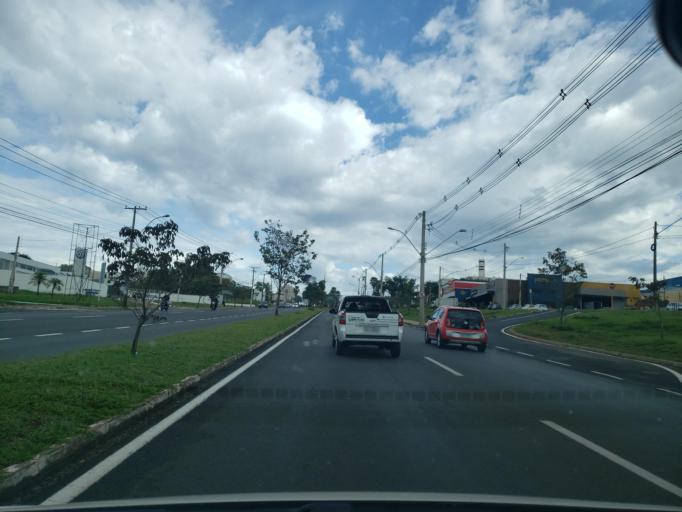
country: BR
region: Sao Paulo
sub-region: Bauru
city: Bauru
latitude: -22.3380
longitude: -49.0422
